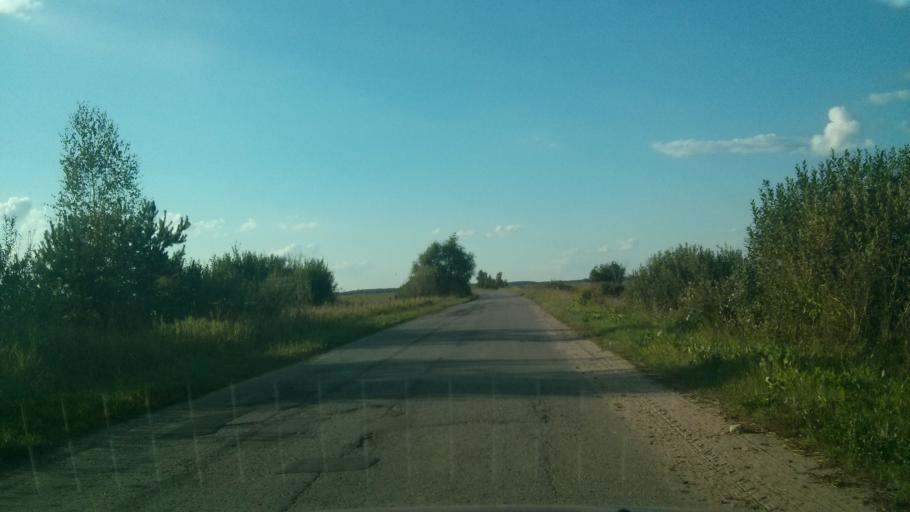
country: RU
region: Vladimir
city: Melenki
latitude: 55.2956
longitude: 41.7953
